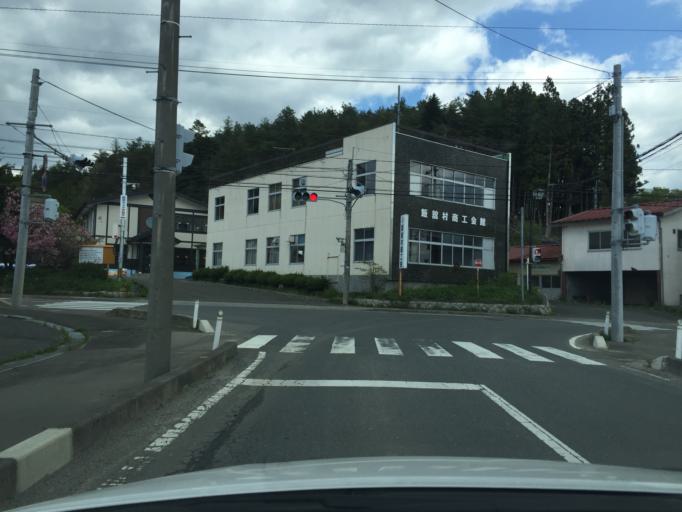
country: JP
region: Fukushima
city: Yanagawamachi-saiwaicho
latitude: 37.6954
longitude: 140.7467
